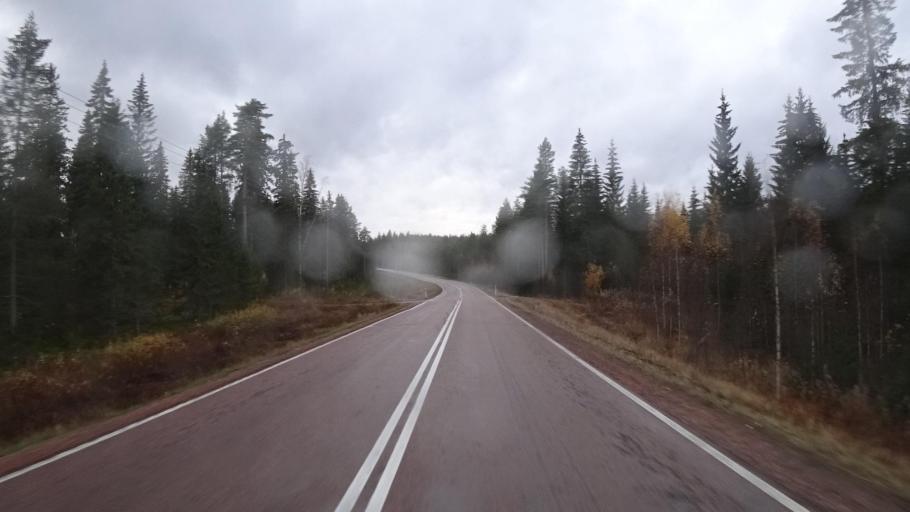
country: FI
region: Southern Savonia
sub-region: Mikkeli
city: Kangasniemi
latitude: 62.0919
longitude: 26.7116
